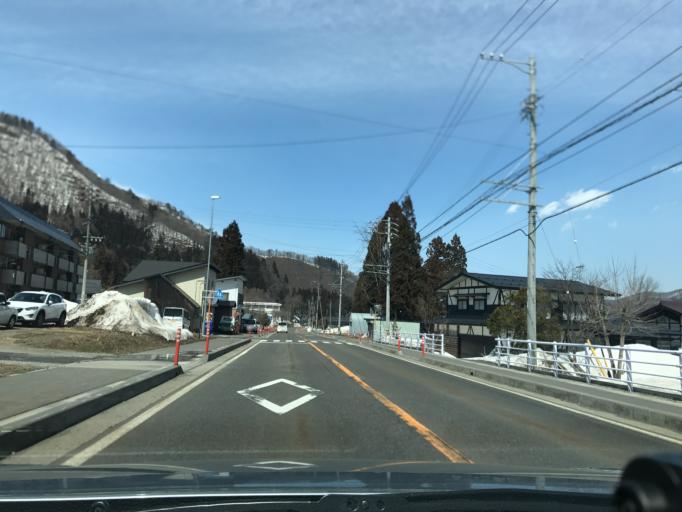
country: JP
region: Nagano
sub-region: Kitaazumi Gun
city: Hakuba
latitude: 36.6426
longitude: 137.8447
